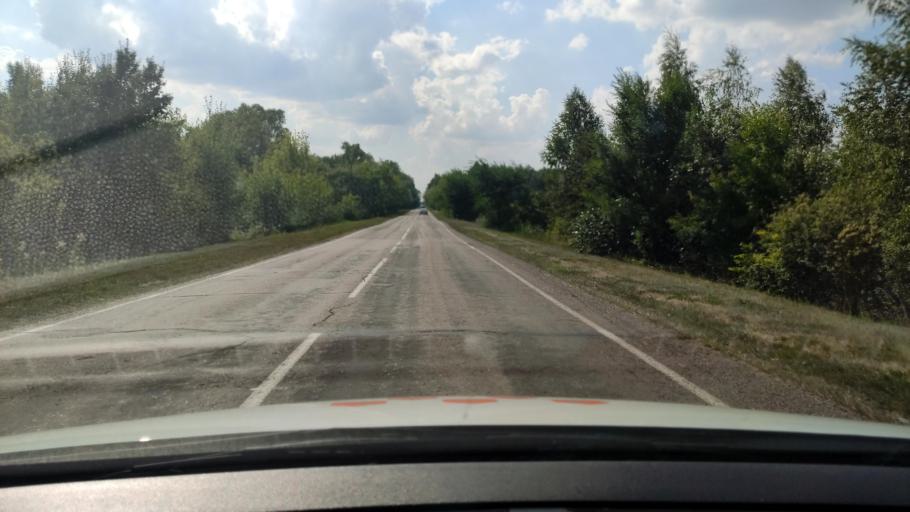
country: RU
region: Voronezj
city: Ertil'
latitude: 51.7839
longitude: 40.5678
